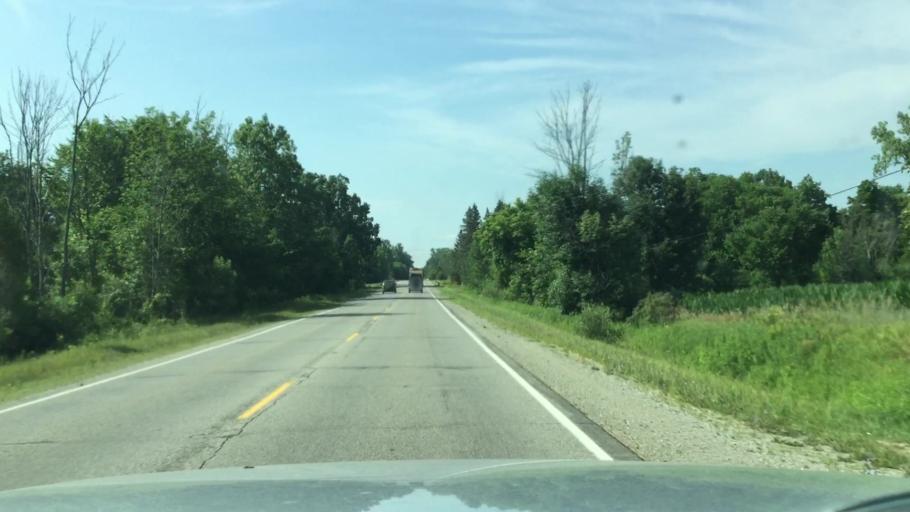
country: US
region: Michigan
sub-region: Genesee County
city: Flushing
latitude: 43.1271
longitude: -83.8138
